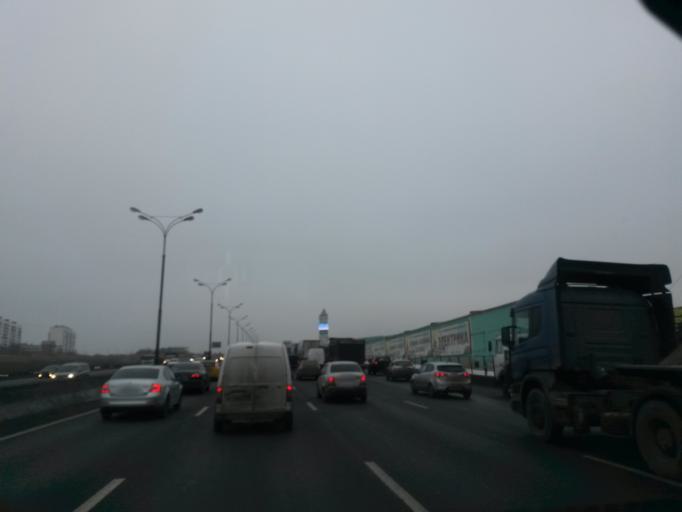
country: RU
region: Moscow
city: Tyoply Stan
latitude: 55.6175
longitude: 37.4844
